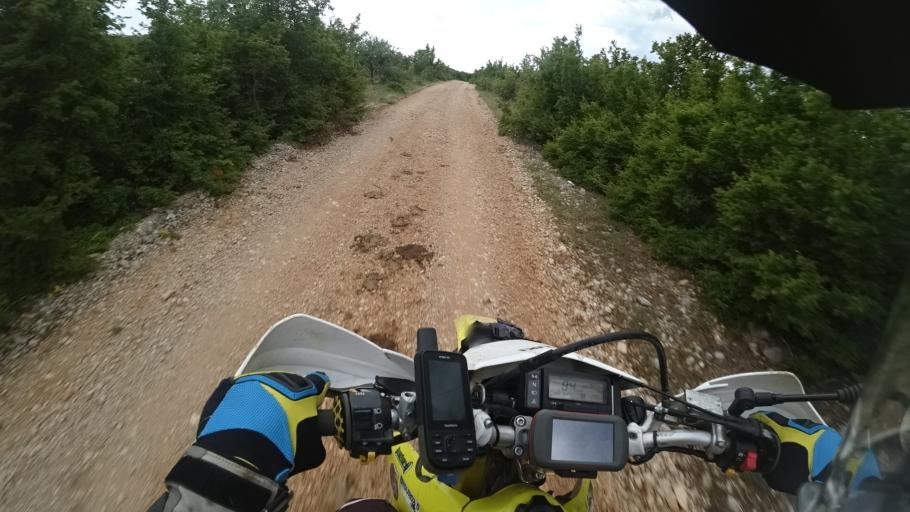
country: HR
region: Sibensko-Kniniska
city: Kistanje
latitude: 44.0938
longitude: 15.9973
